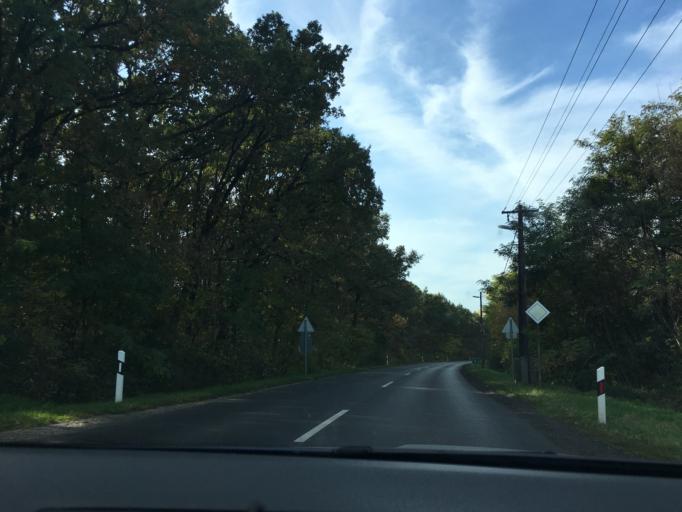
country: HU
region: Hajdu-Bihar
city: Vamospercs
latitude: 47.5233
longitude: 21.8762
